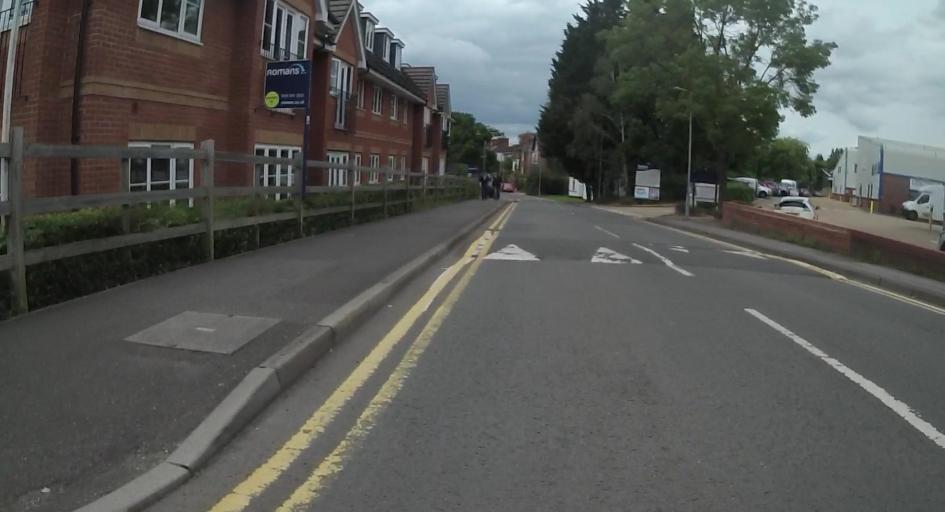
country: GB
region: England
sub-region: Wokingham
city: Wokingham
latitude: 51.4115
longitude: -0.8433
